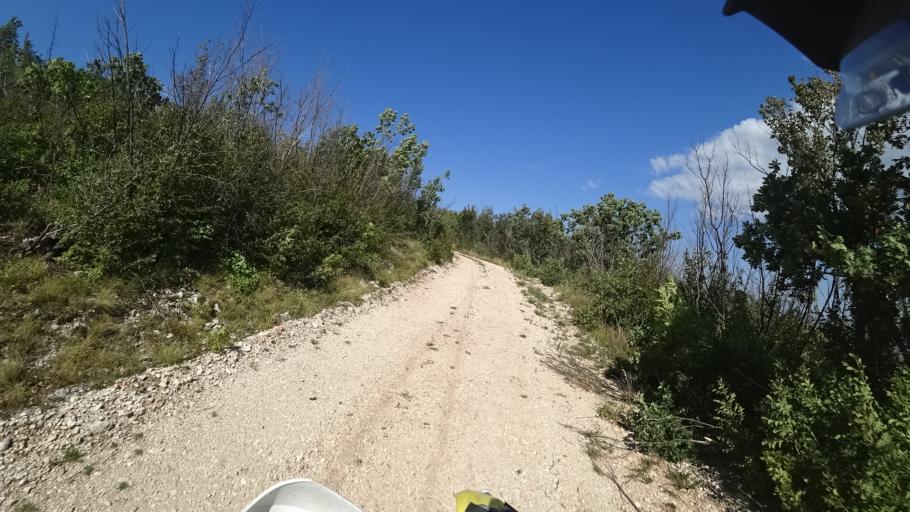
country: HR
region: Sibensko-Kniniska
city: Knin
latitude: 43.9601
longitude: 16.1543
